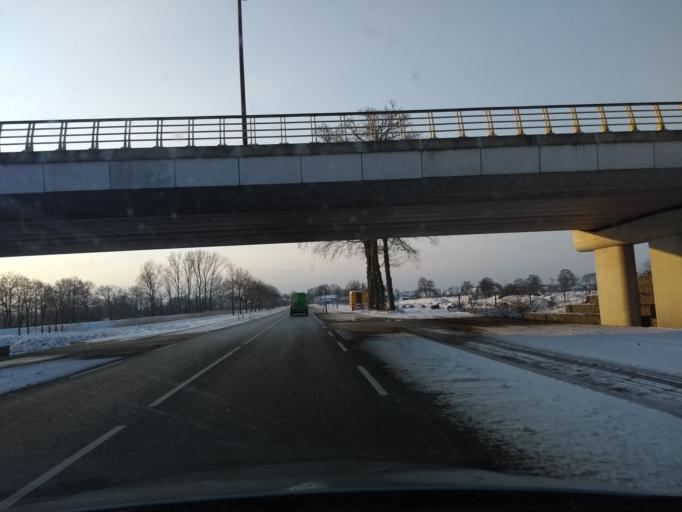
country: NL
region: Overijssel
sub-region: Gemeente Almelo
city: Almelo
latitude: 52.3186
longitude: 6.6546
